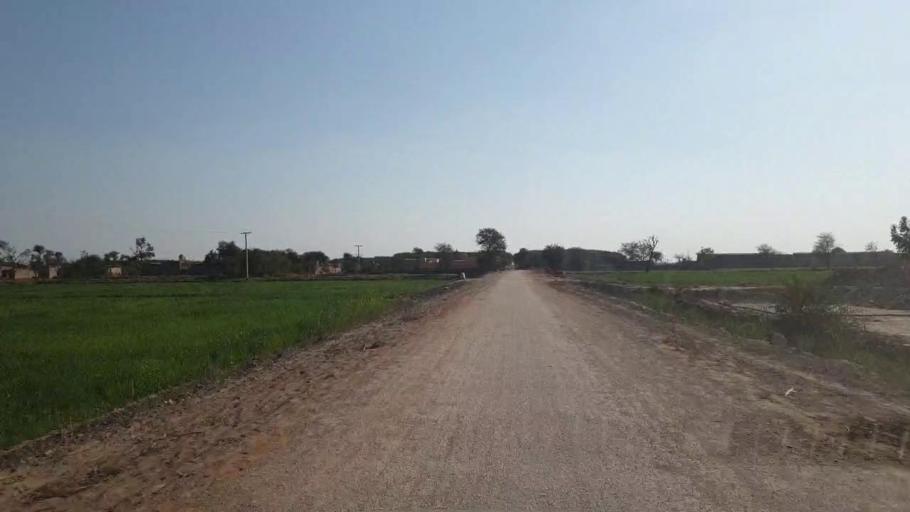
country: PK
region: Sindh
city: Tando Allahyar
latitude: 25.4061
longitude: 68.7054
